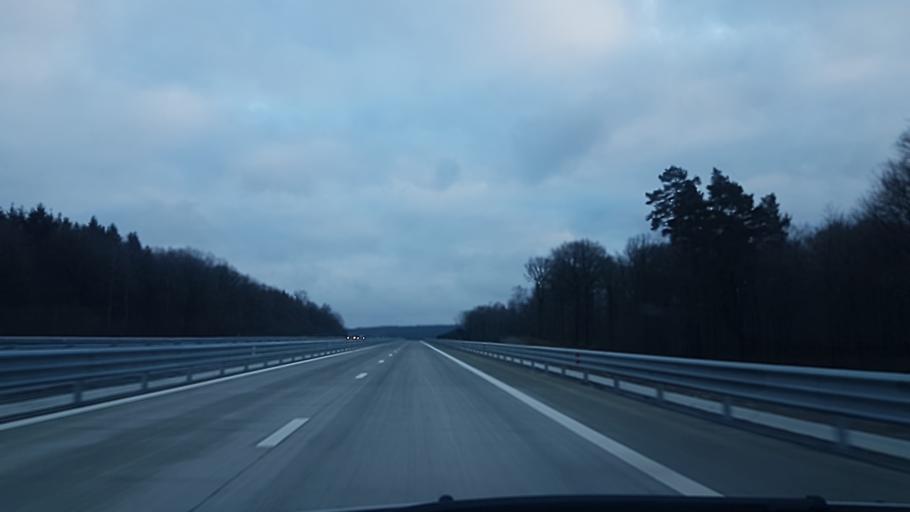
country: BE
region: Wallonia
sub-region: Province de Namur
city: Couvin
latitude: 50.0200
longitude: 4.5269
